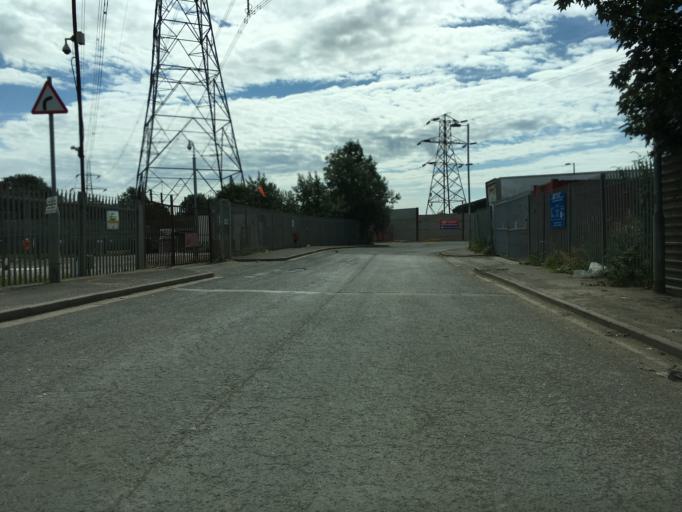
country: GB
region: Wales
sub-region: Newport
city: Newport
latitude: 51.5674
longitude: -2.9751
